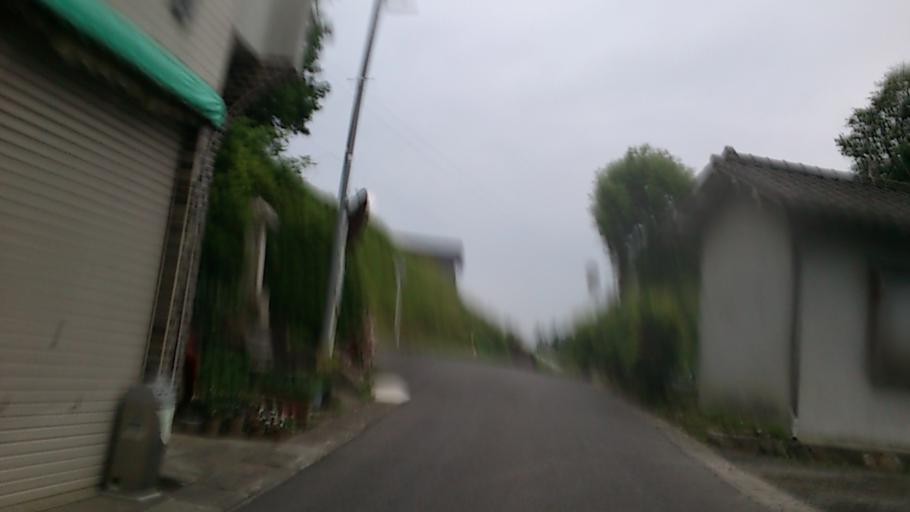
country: JP
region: Fukushima
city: Fukushima-shi
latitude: 37.6677
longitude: 140.5082
